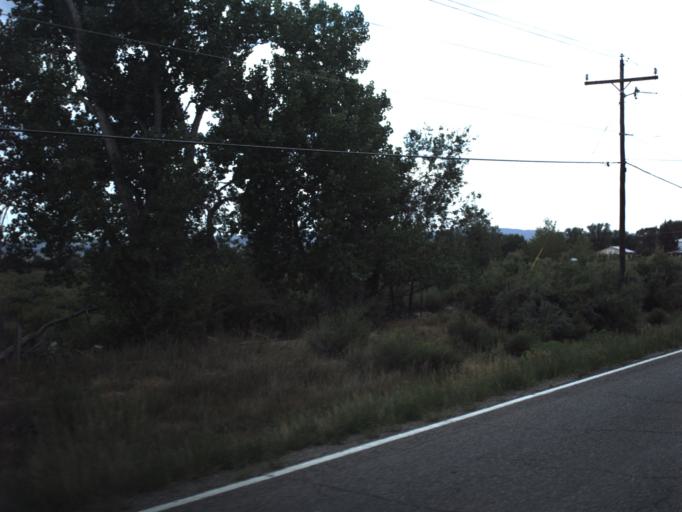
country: US
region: Utah
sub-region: Emery County
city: Huntington
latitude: 39.3552
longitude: -110.8520
